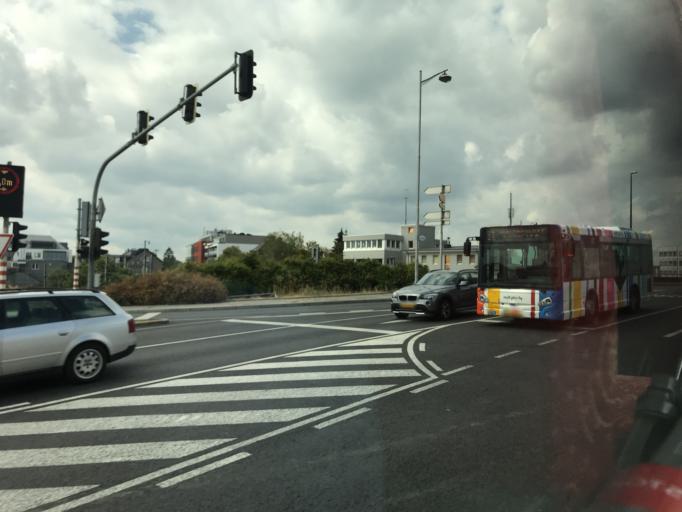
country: LU
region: Luxembourg
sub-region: Canton de Luxembourg
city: Luxembourg
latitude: 49.5954
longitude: 6.1334
